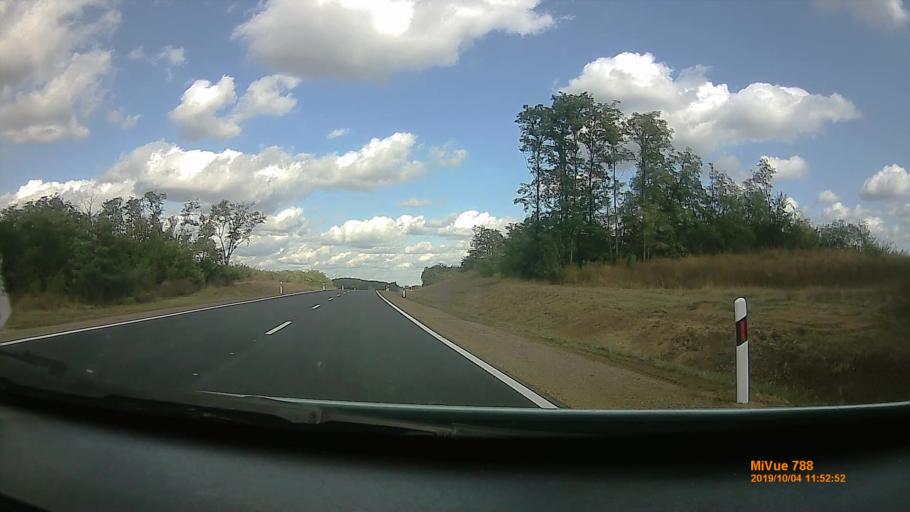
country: HU
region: Szabolcs-Szatmar-Bereg
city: Nyirtelek
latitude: 48.0030
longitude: 21.6733
